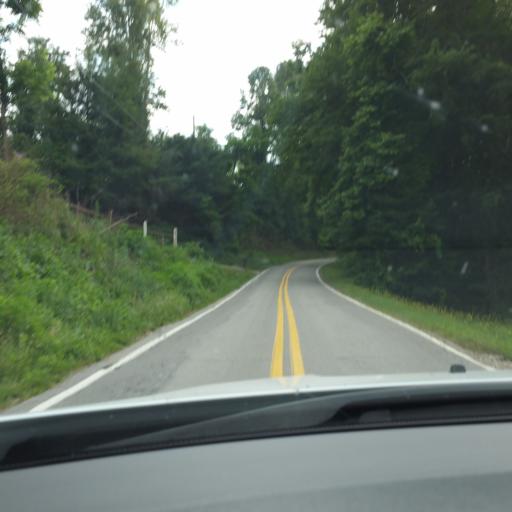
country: US
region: North Carolina
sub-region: Buncombe County
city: Bent Creek
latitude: 35.5223
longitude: -82.6853
